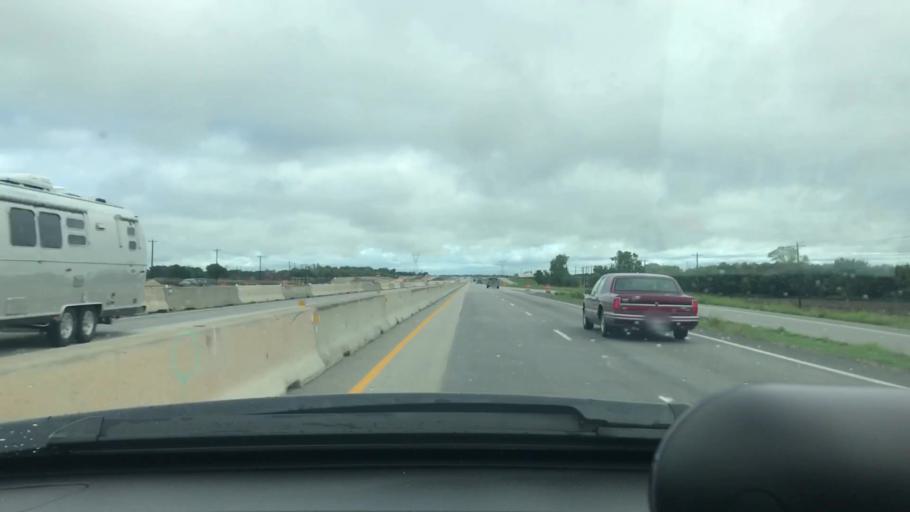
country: US
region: Texas
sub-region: Collin County
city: Anna
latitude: 33.3565
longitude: -96.5843
